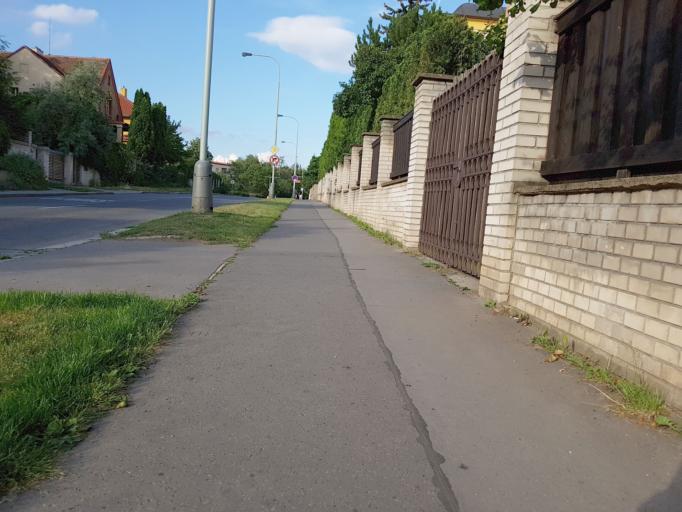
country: CZ
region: Praha
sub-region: Praha 8
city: Liben
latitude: 50.0708
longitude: 14.4966
